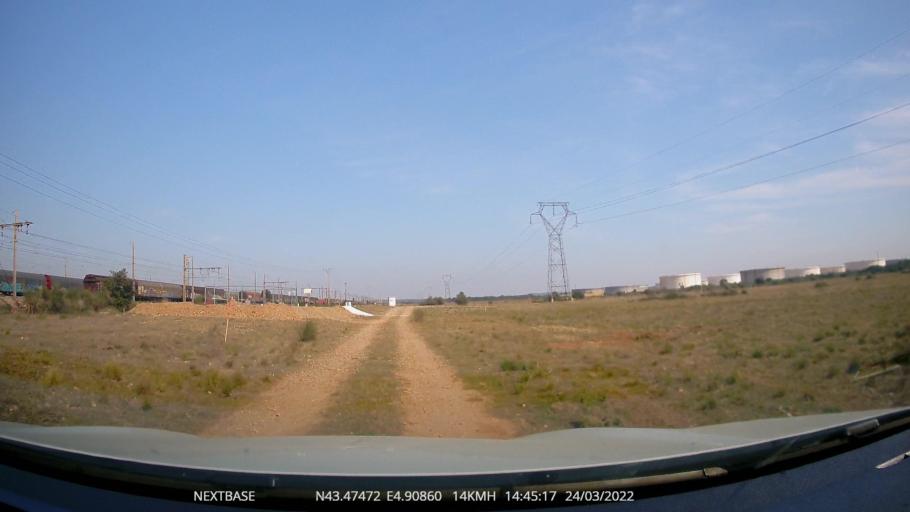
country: FR
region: Provence-Alpes-Cote d'Azur
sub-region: Departement des Bouches-du-Rhone
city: Fos-sur-Mer
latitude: 43.4740
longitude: 4.9078
